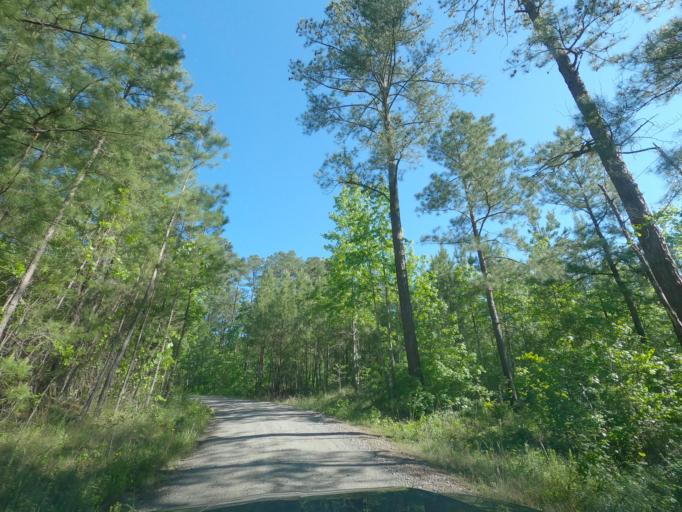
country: US
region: Georgia
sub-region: Columbia County
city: Evans
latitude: 33.6137
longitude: -82.1124
